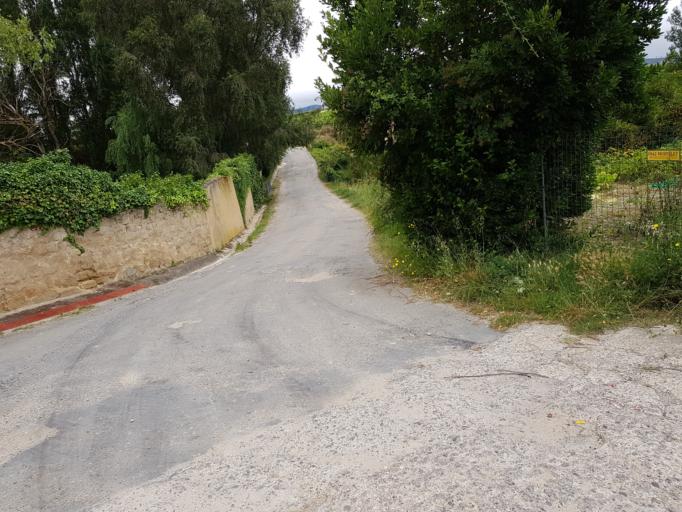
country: ES
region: La Rioja
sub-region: Provincia de La Rioja
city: Sajazarra
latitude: 42.5896
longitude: -2.9595
